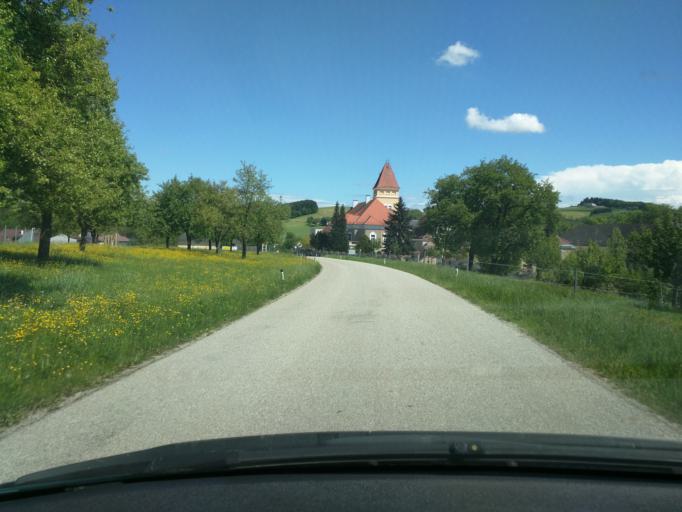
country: AT
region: Lower Austria
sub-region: Politischer Bezirk Amstetten
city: Sankt Georgen am Ybbsfelde
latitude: 48.1616
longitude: 14.9228
